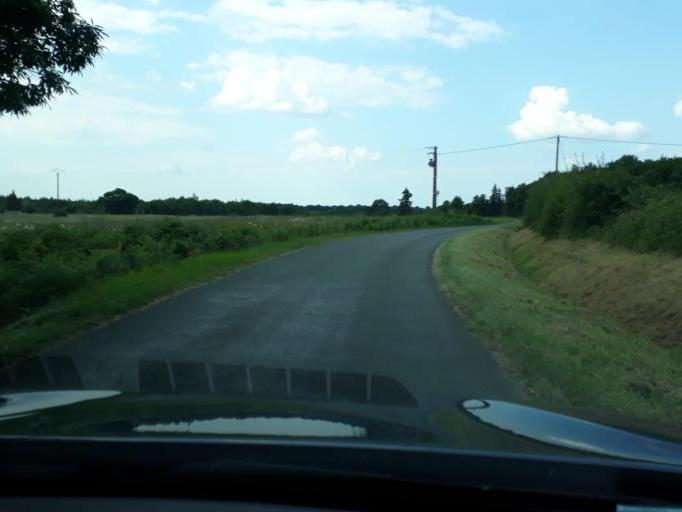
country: FR
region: Centre
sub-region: Departement du Cher
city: Jouet-sur-l'Aubois
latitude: 46.9657
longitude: 2.9458
